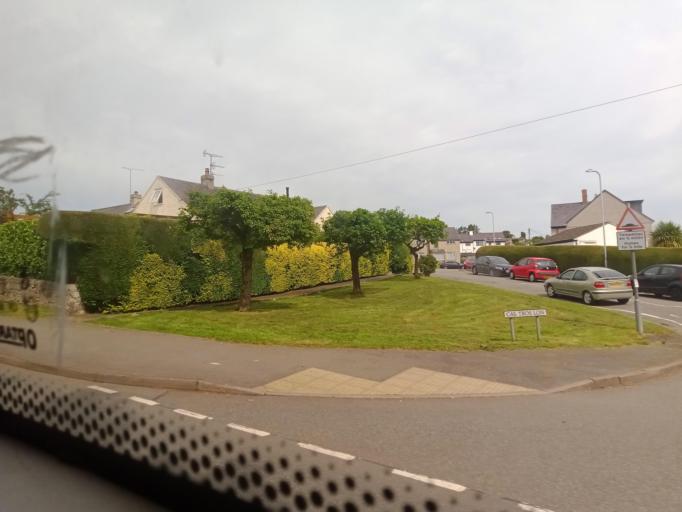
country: GB
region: Wales
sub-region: Anglesey
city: Menai Bridge
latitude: 53.2289
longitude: -4.1738
